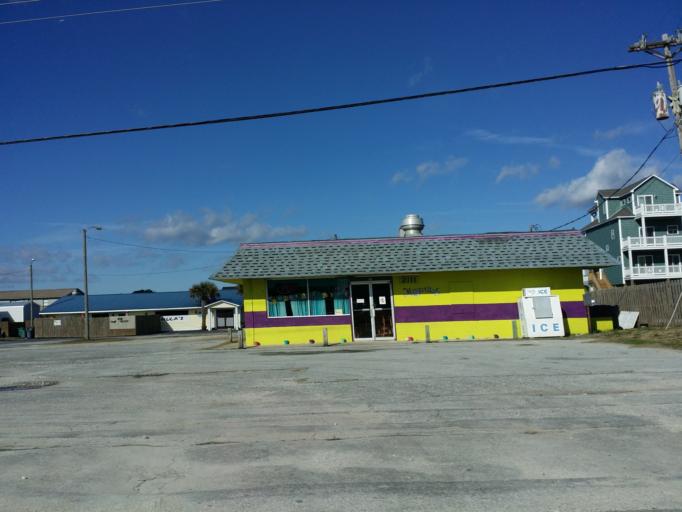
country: US
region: North Carolina
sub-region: Pender County
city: Surf City
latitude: 34.4467
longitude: -77.5111
